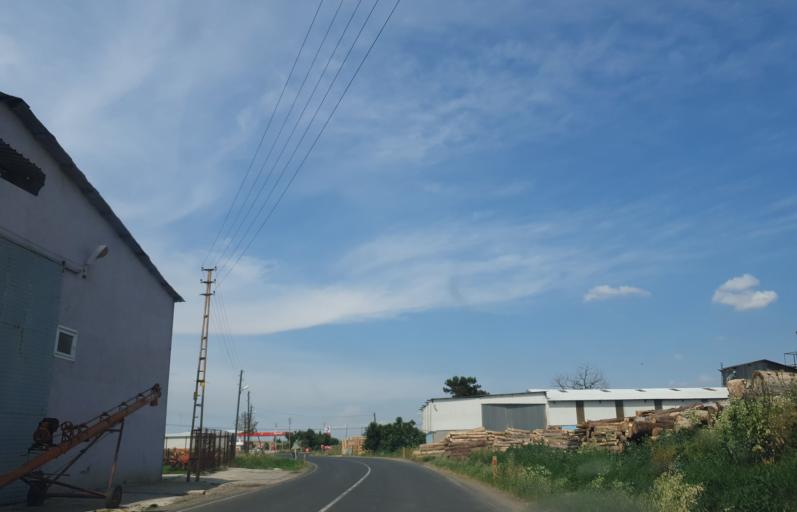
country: TR
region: Tekirdag
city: Muratli
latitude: 41.2209
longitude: 27.5478
